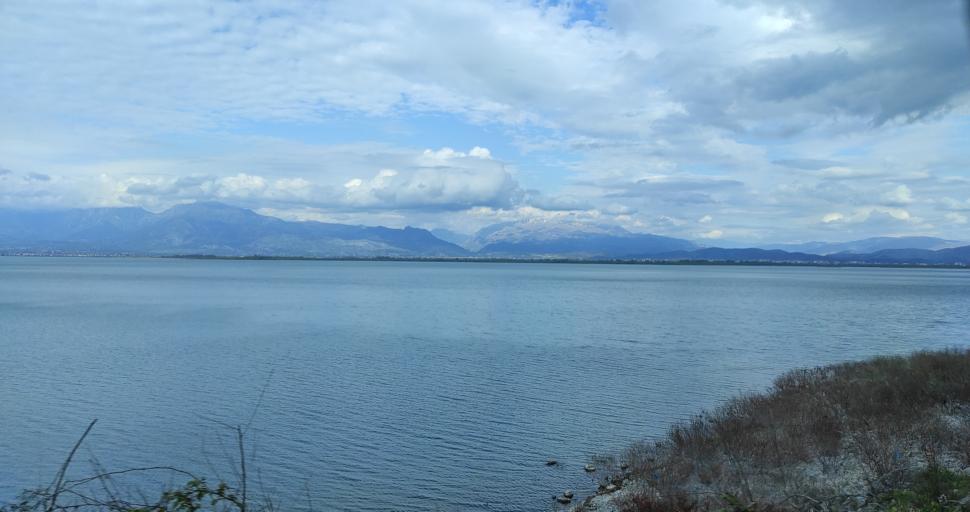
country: AL
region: Shkoder
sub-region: Rrethi i Shkodres
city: Berdica e Madhe
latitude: 42.0661
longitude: 19.4298
